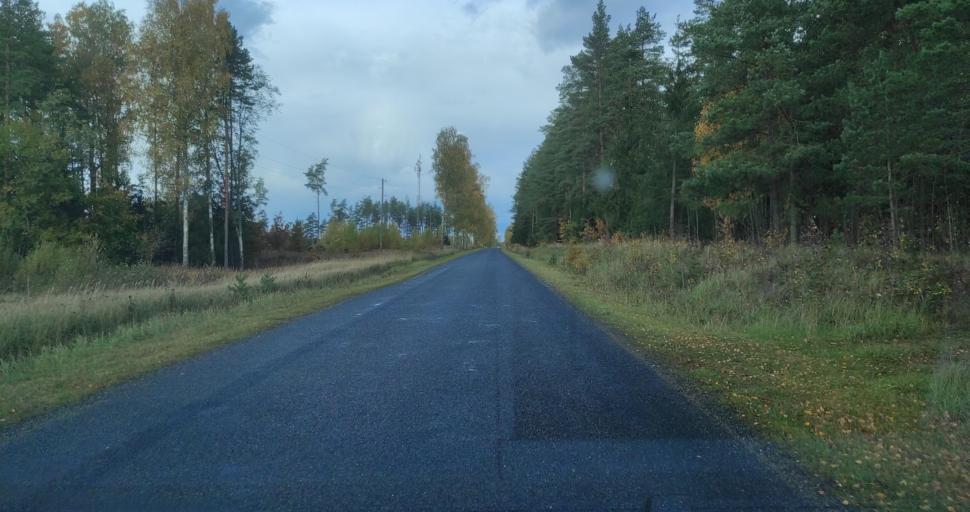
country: LV
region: Skrunda
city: Skrunda
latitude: 56.6837
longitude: 22.0643
